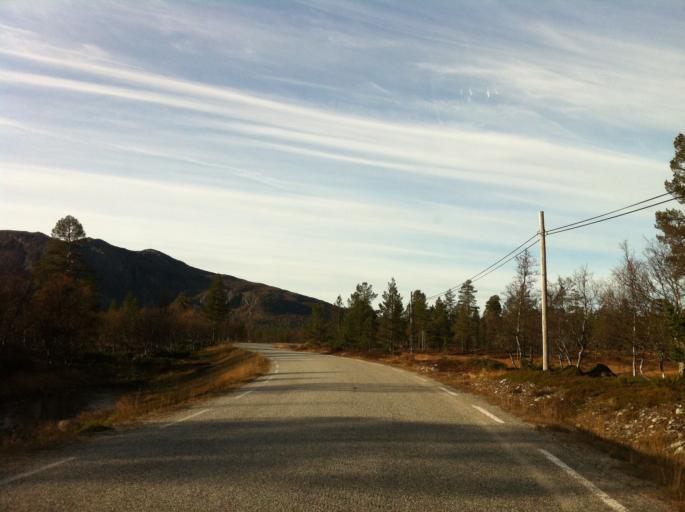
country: NO
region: Hedmark
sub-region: Engerdal
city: Engerdal
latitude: 62.0870
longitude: 12.0579
